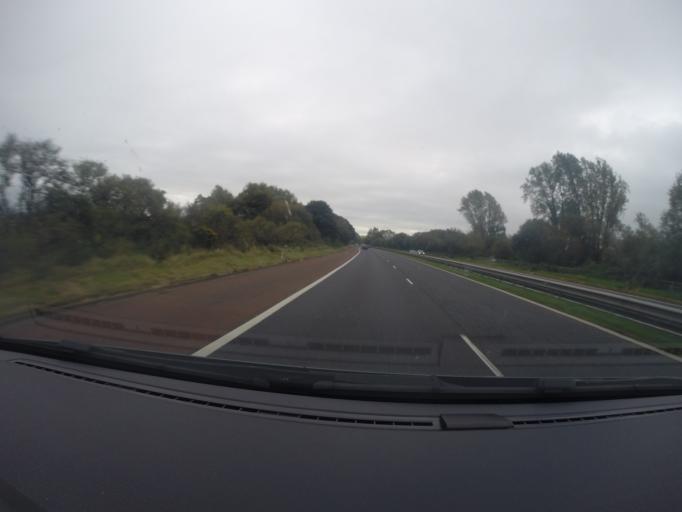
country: GB
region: Northern Ireland
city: Hillsborough
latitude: 54.4698
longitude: -6.1518
